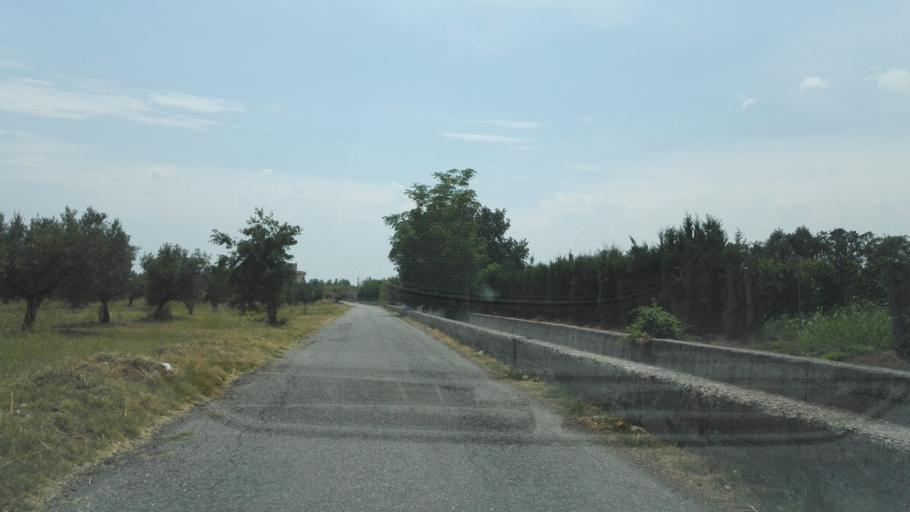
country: IT
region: Calabria
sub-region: Provincia di Reggio Calabria
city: Monasterace Marina
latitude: 38.4339
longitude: 16.5578
